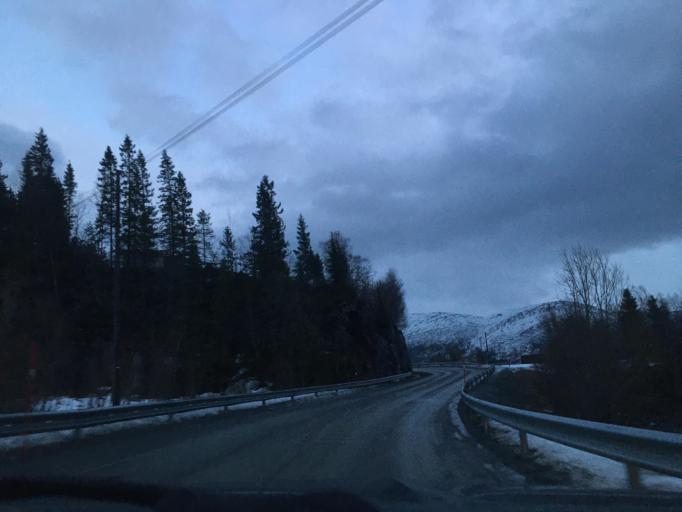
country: NO
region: Nordland
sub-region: Rana
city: Hauknes
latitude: 66.3049
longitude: 13.9492
